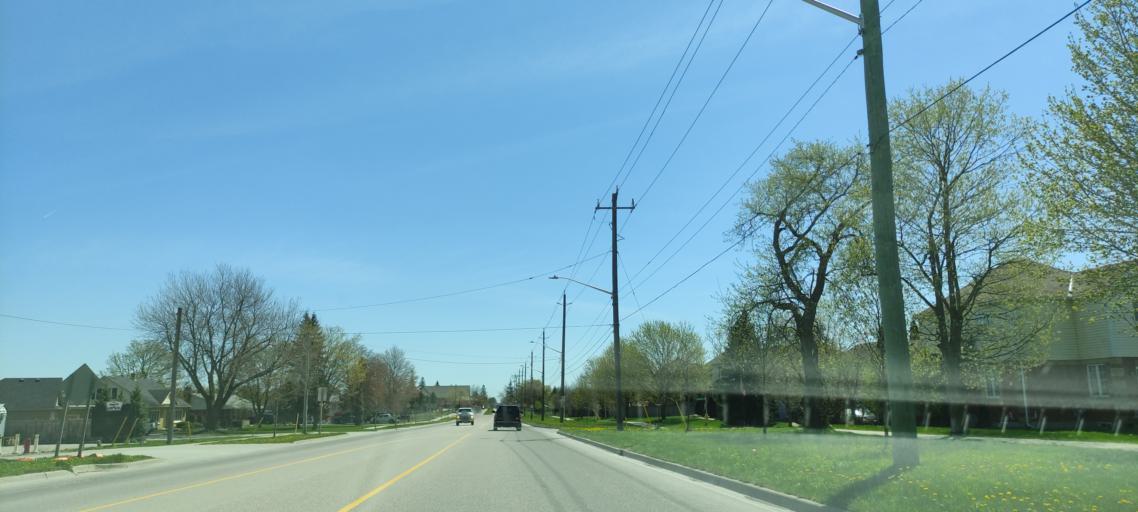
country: CA
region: Ontario
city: Waterloo
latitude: 43.6011
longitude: -80.5707
